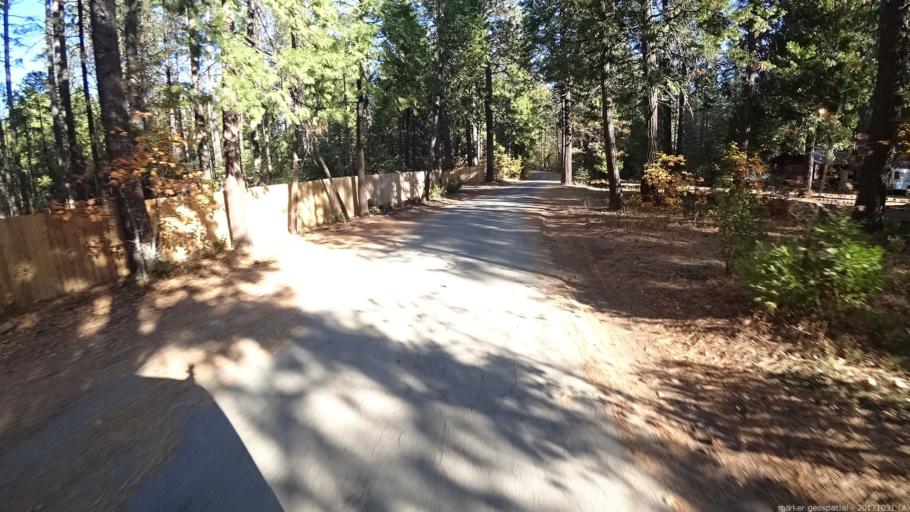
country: US
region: California
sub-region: Shasta County
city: Shingletown
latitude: 40.4901
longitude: -121.8608
